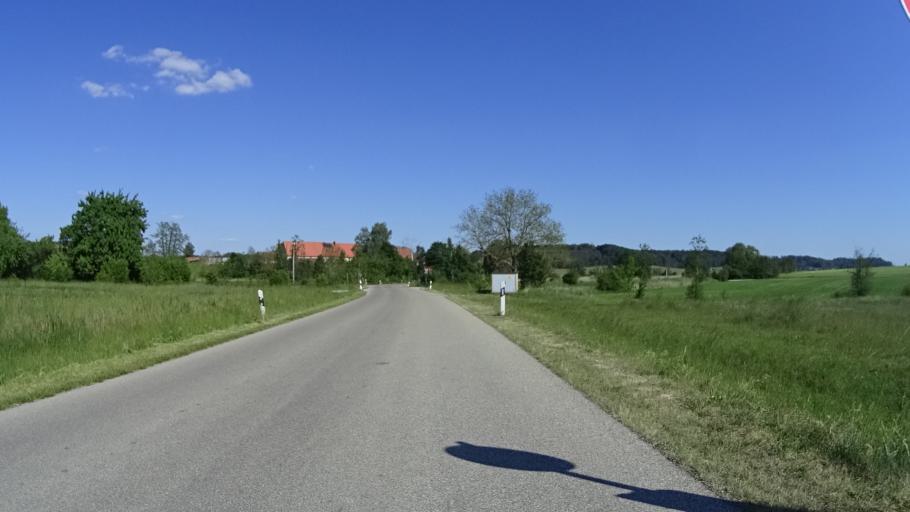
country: DE
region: Bavaria
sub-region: Regierungsbezirk Mittelfranken
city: Feuchtwangen
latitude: 49.2068
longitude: 10.3161
